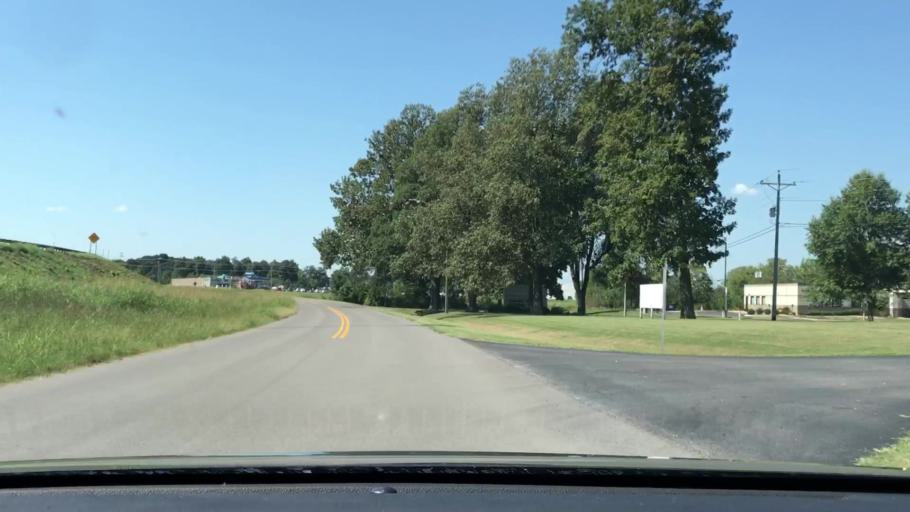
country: US
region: Kentucky
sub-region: Fulton County
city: Fulton
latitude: 36.5178
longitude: -88.8951
